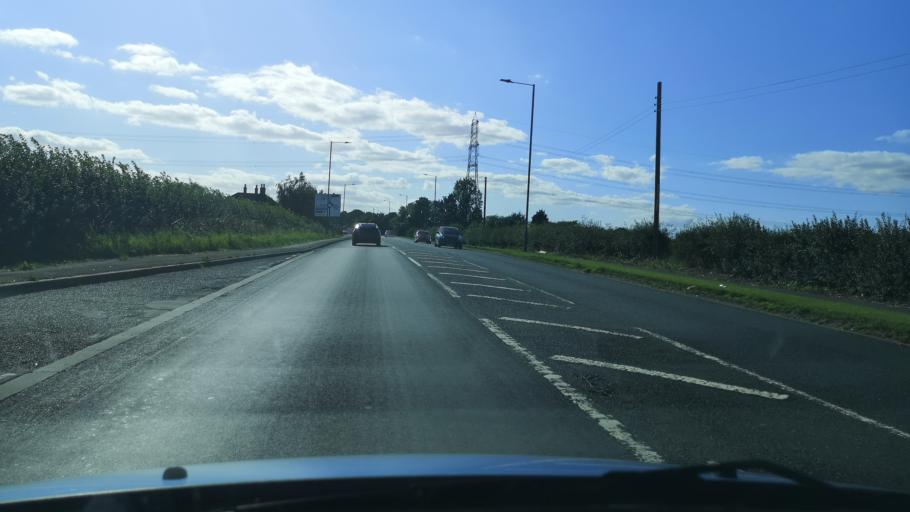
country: GB
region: England
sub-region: Doncaster
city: Kirk Sandall
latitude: 53.5568
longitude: -1.0487
